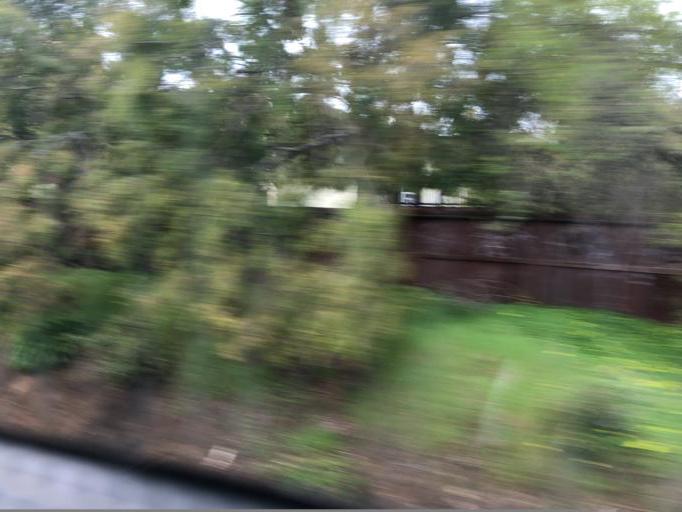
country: US
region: California
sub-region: San Mateo County
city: San Mateo
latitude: 37.5753
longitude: -122.3332
